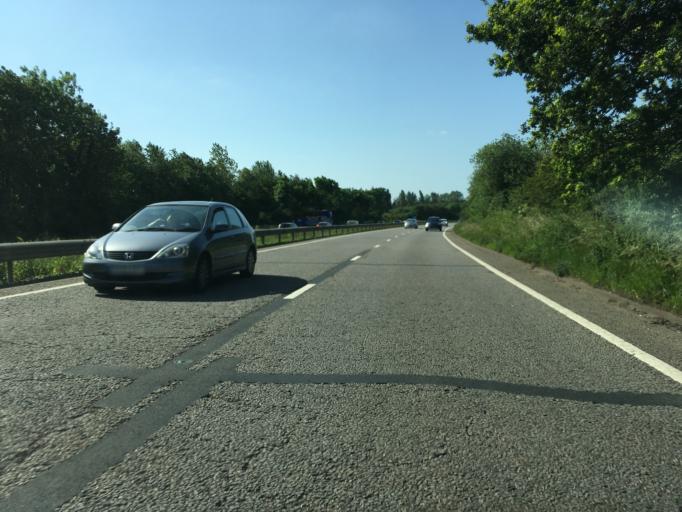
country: GB
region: England
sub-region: Milton Keynes
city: Water Eaton
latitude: 51.9971
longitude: -0.7059
